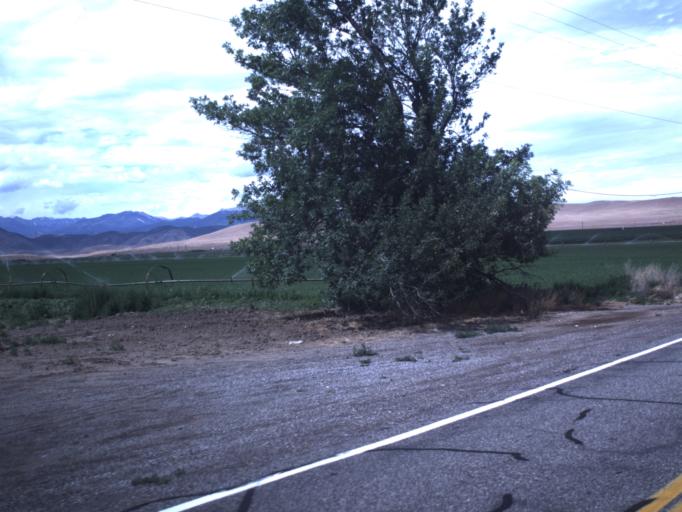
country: US
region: Utah
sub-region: Sevier County
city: Monroe
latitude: 38.6290
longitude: -112.1486
